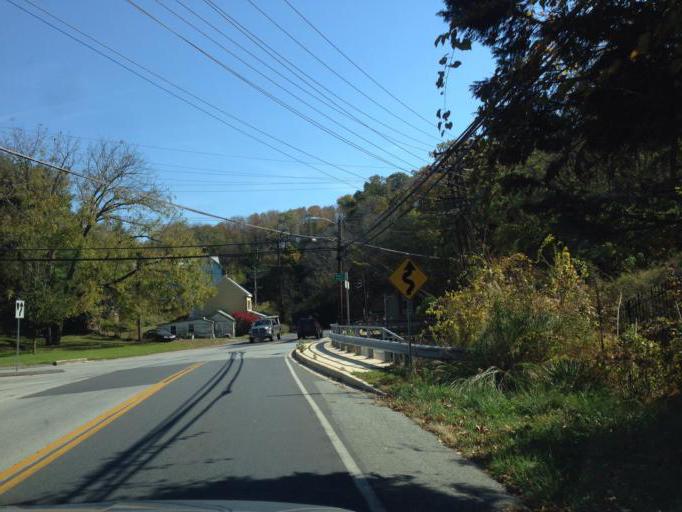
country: US
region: Maryland
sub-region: Howard County
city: Ellicott City
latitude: 39.2692
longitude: -76.8107
